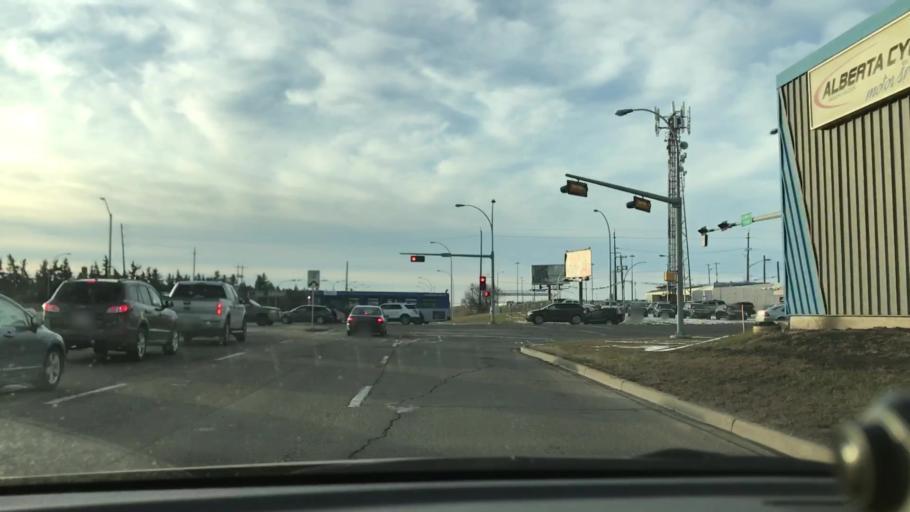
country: CA
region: Alberta
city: Edmonton
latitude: 53.5816
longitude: -113.4912
